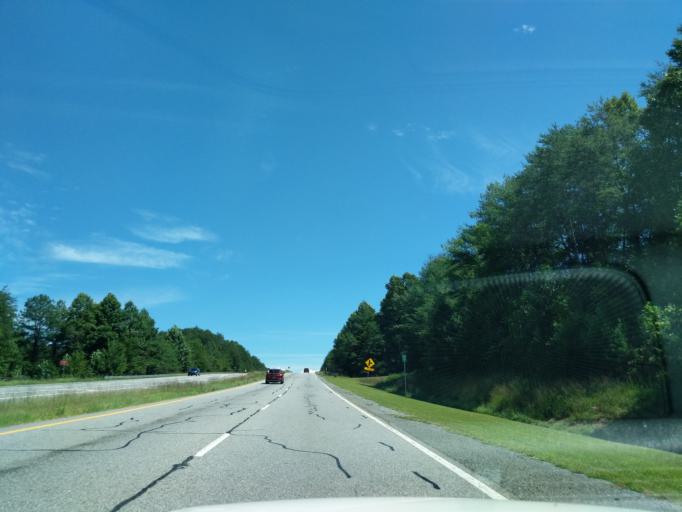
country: US
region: Georgia
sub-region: Fannin County
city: Blue Ridge
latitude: 34.8926
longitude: -84.2474
